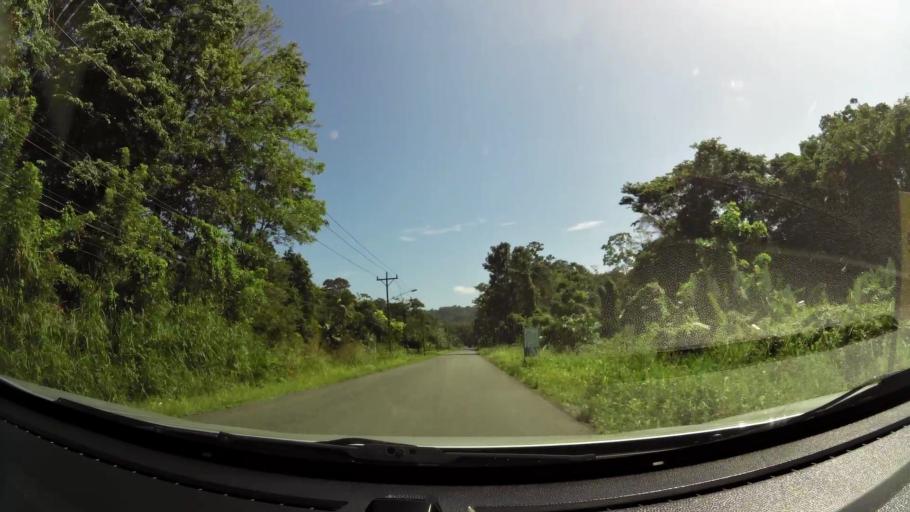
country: PA
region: Bocas del Toro
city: Barranco
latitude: 9.6516
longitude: -82.7939
